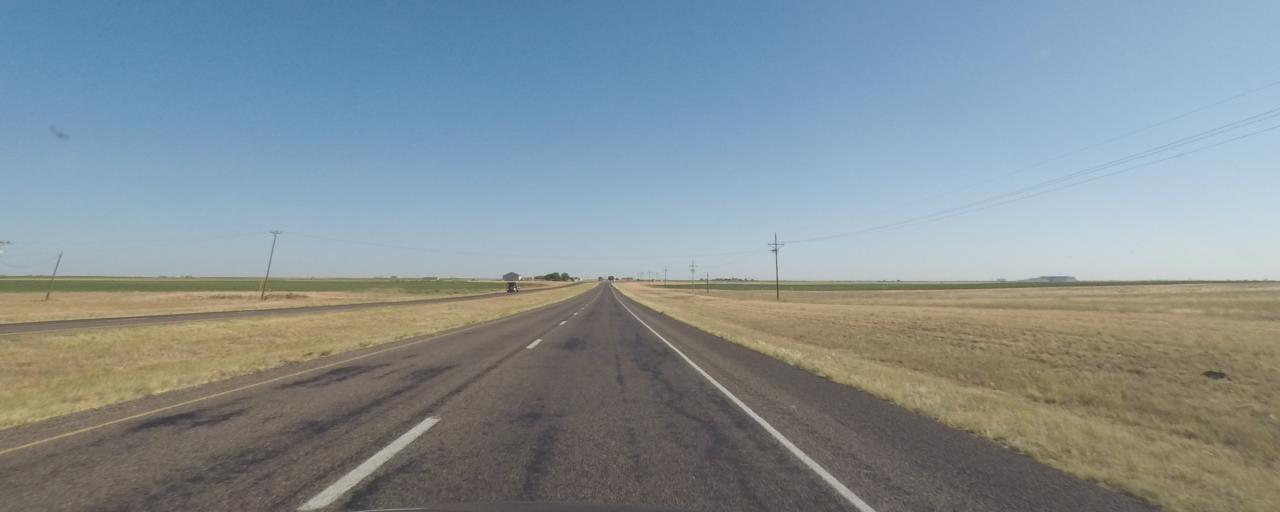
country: US
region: Texas
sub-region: Gaines County
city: Seagraves
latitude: 32.8631
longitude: -102.6403
